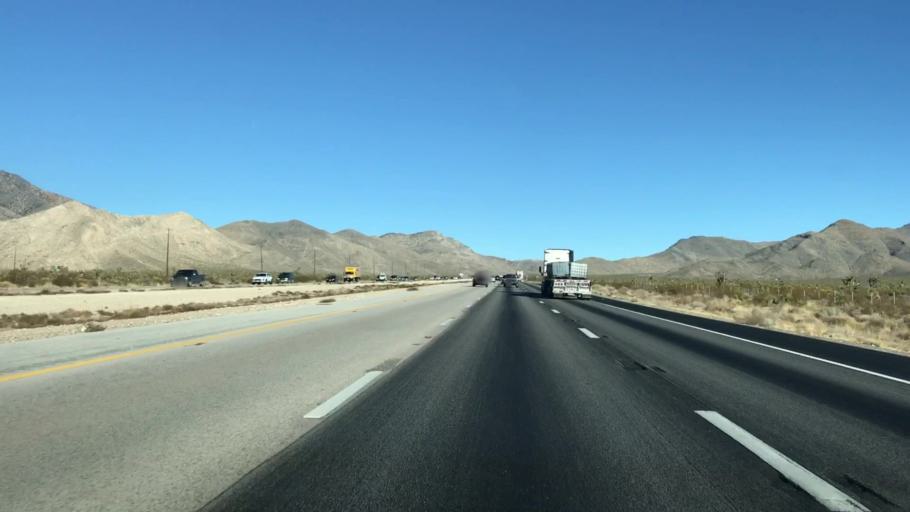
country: US
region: Nevada
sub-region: Clark County
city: Sandy Valley
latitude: 35.4605
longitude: -115.6254
